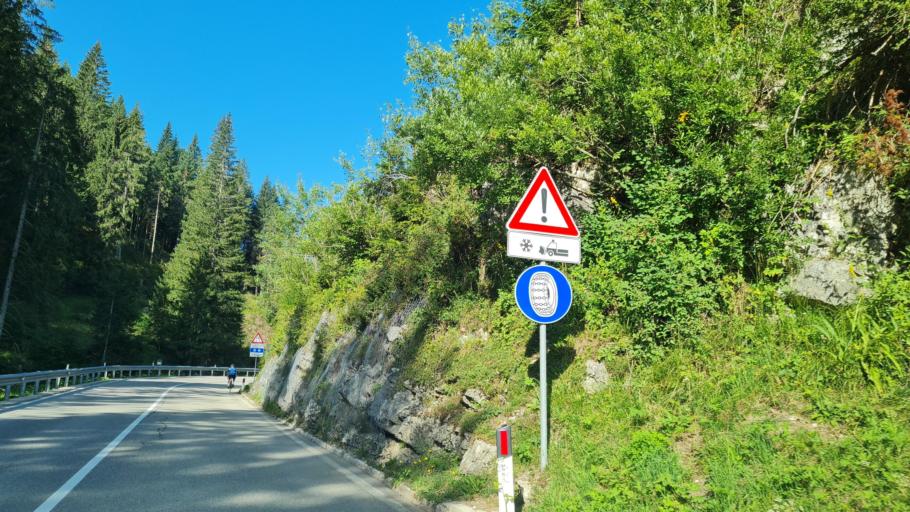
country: IT
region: Trentino-Alto Adige
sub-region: Provincia di Trento
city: Luserna
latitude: 45.9511
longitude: 11.3834
